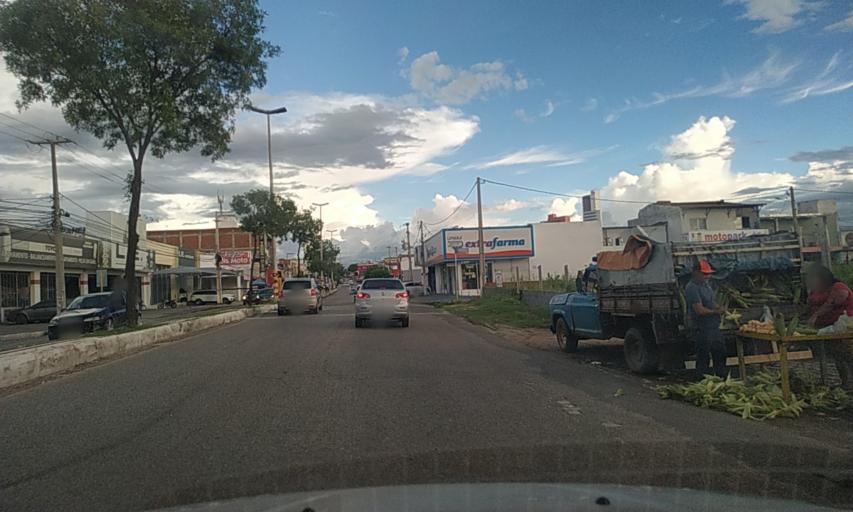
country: BR
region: Rio Grande do Norte
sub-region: Mossoro
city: Mossoro
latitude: -5.2039
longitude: -37.3371
